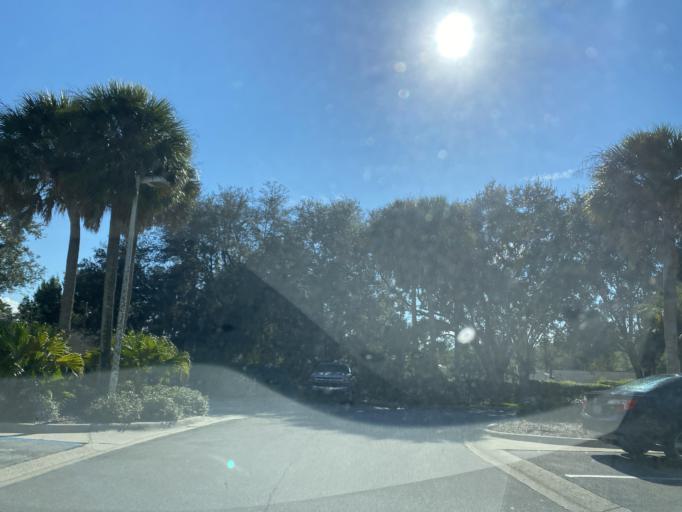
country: US
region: Florida
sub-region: Marion County
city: Ocala
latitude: 29.0546
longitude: -82.2579
